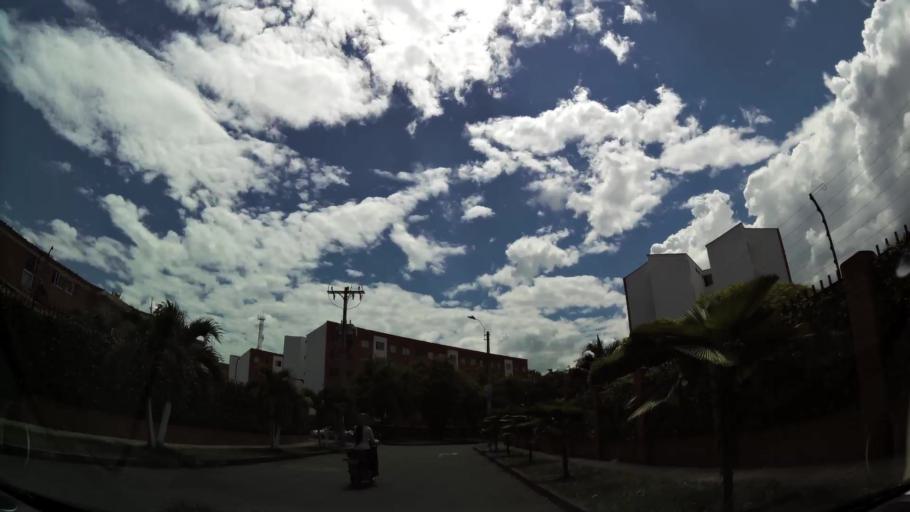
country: CO
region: Valle del Cauca
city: Cali
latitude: 3.3840
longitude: -76.5195
